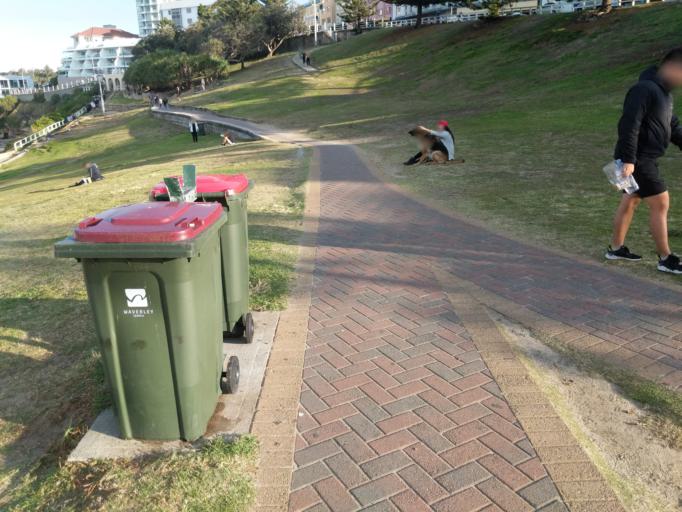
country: AU
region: New South Wales
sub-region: Waverley
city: Bondi Beach
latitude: -33.8928
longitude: 151.2734
